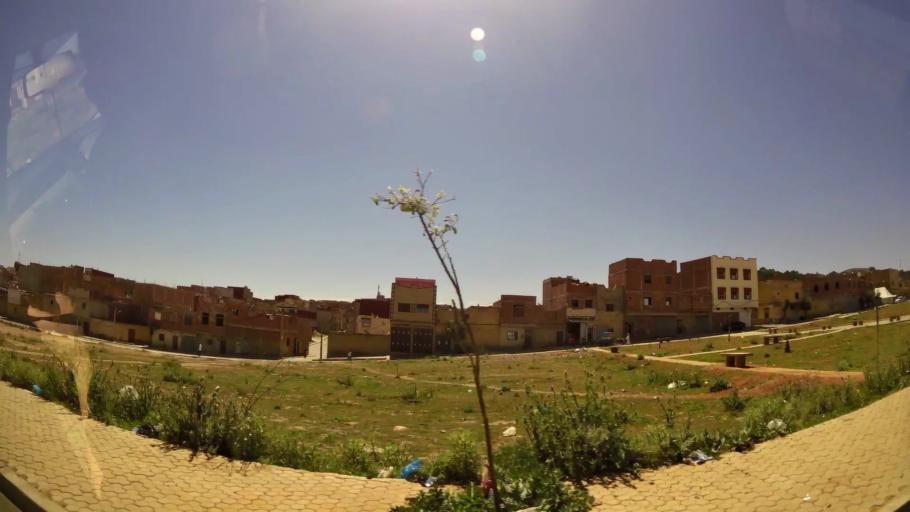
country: MA
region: Oriental
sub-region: Oujda-Angad
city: Oujda
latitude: 34.6509
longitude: -1.8768
